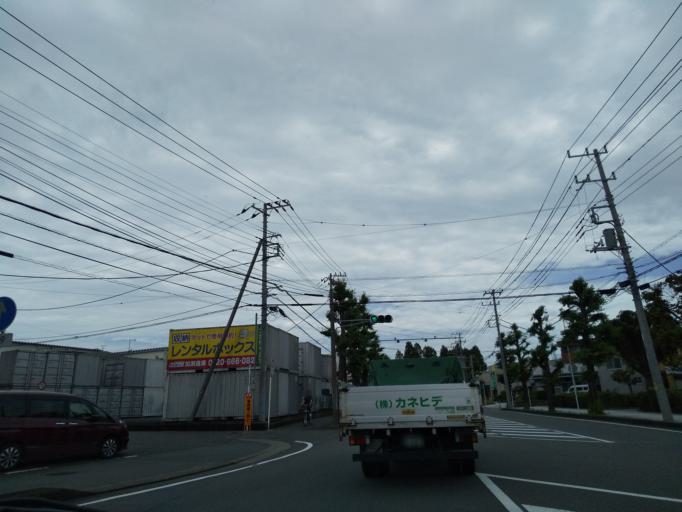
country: JP
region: Kanagawa
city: Zama
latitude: 35.5093
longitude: 139.3596
